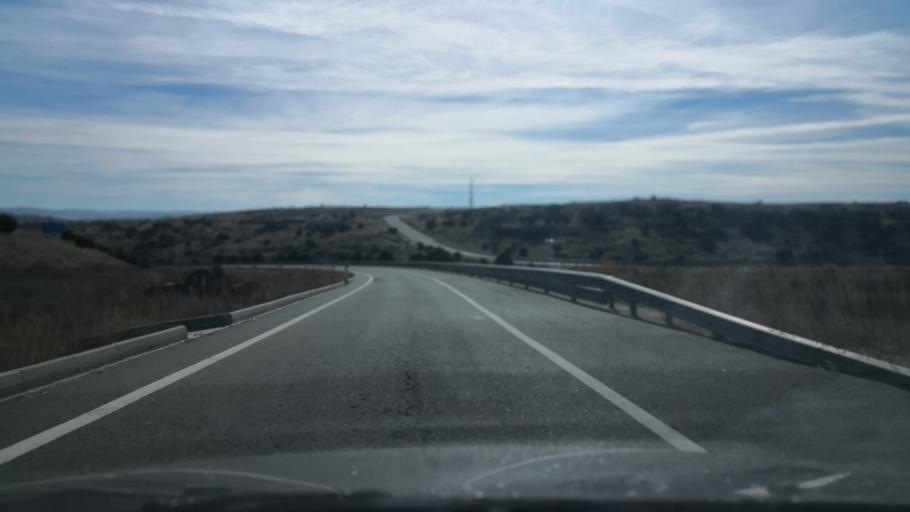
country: ES
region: Castille and Leon
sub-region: Provincia de Avila
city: Avila
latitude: 40.6727
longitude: -4.7267
